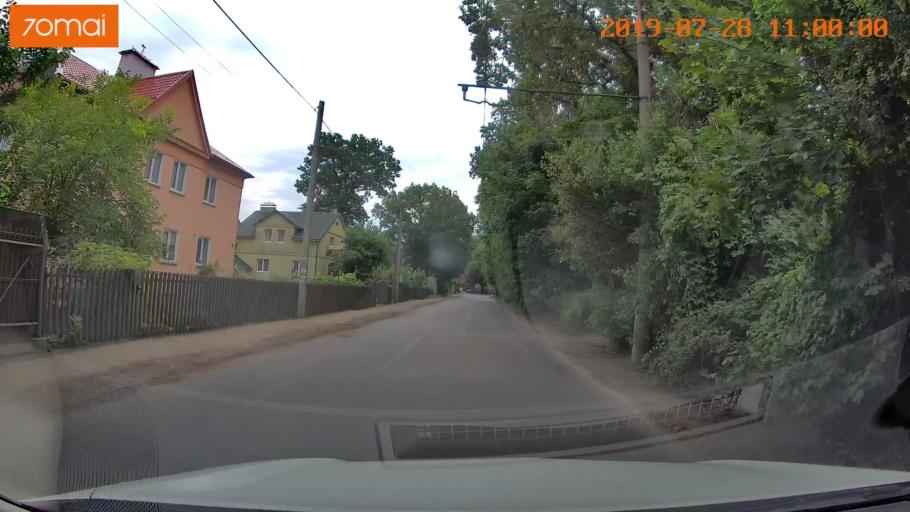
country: RU
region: Kaliningrad
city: Vzmorye
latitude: 54.7269
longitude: 20.3582
